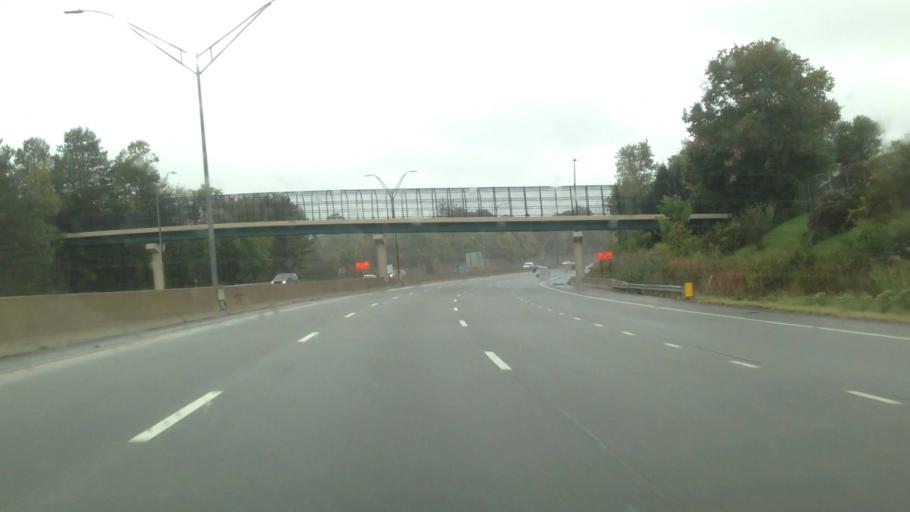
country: US
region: Ohio
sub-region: Summit County
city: Silver Lake
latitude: 41.1604
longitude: -81.4695
